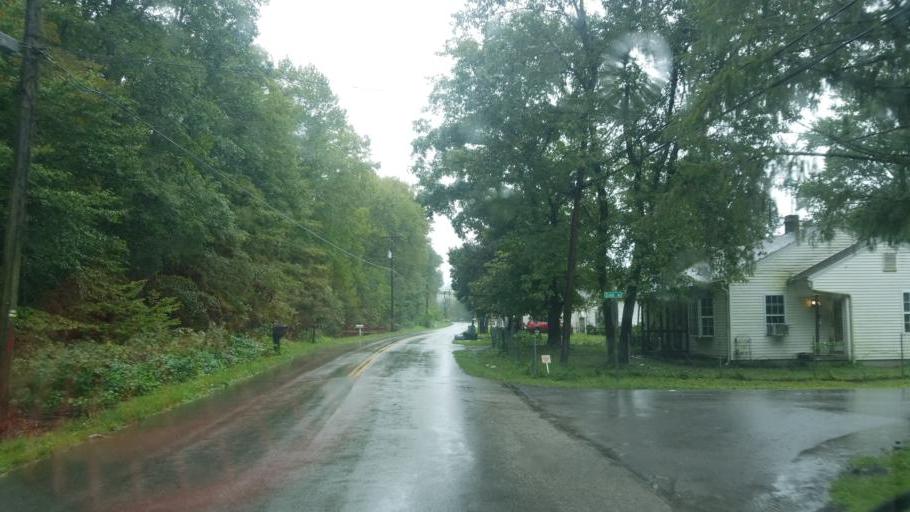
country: US
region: Ohio
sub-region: Scioto County
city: West Portsmouth
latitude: 38.7363
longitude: -83.0667
